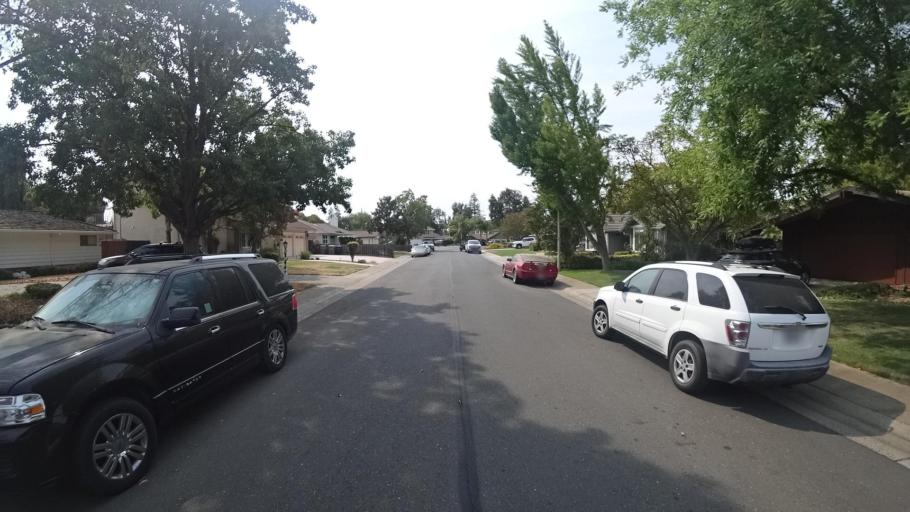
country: US
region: California
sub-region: Sacramento County
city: Elk Grove
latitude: 38.4062
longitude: -121.3728
